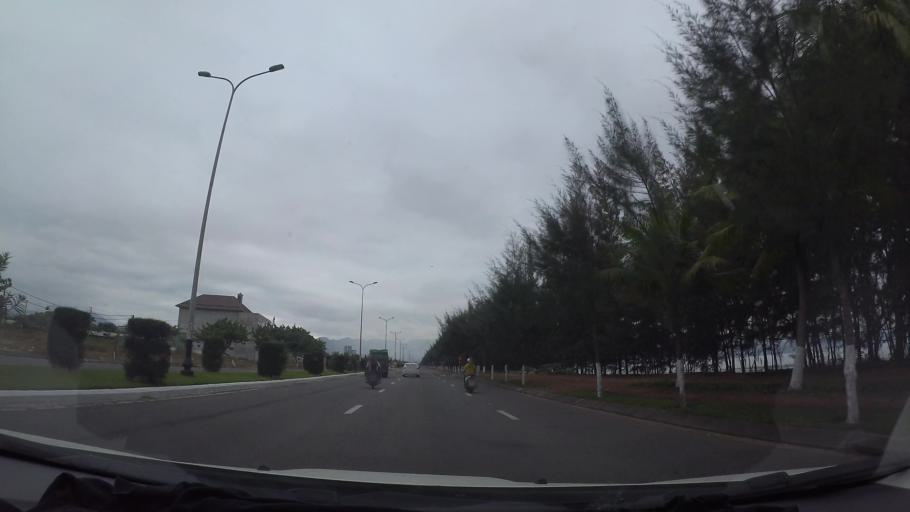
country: VN
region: Da Nang
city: Lien Chieu
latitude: 16.1002
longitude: 108.1410
